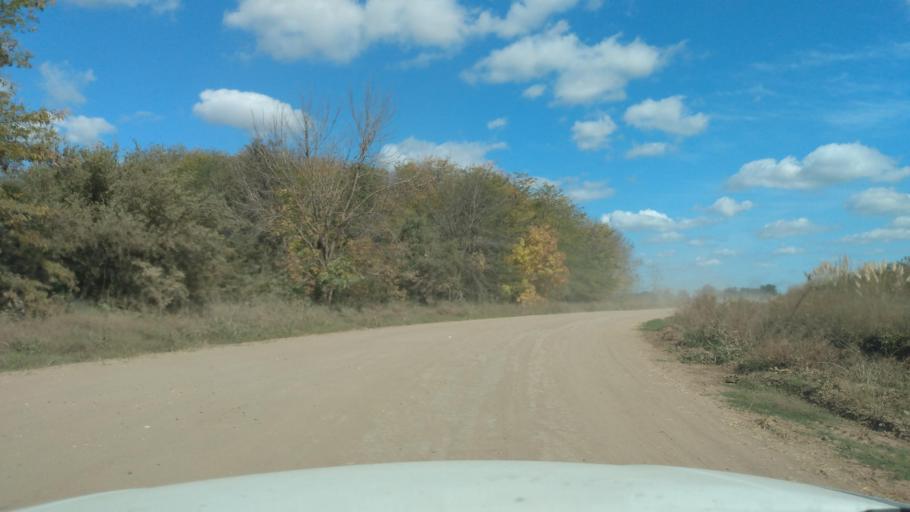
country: AR
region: Buenos Aires
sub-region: Partido de Navarro
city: Navarro
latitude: -35.0175
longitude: -59.4243
